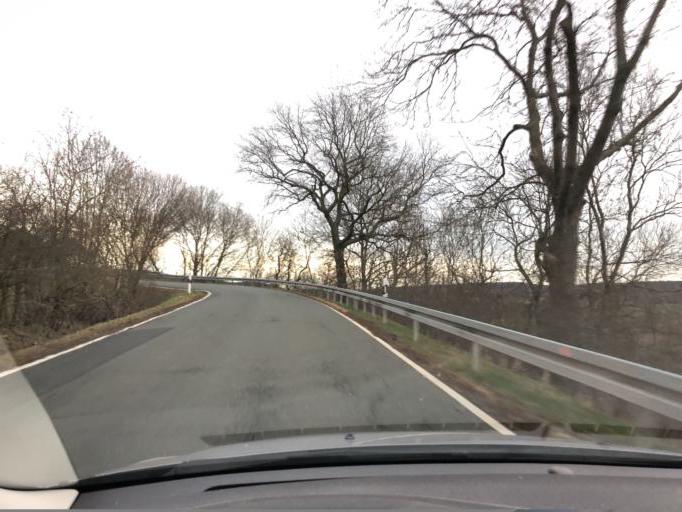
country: DE
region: Saxony-Anhalt
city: Bad Bibra
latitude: 51.1711
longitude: 11.6140
